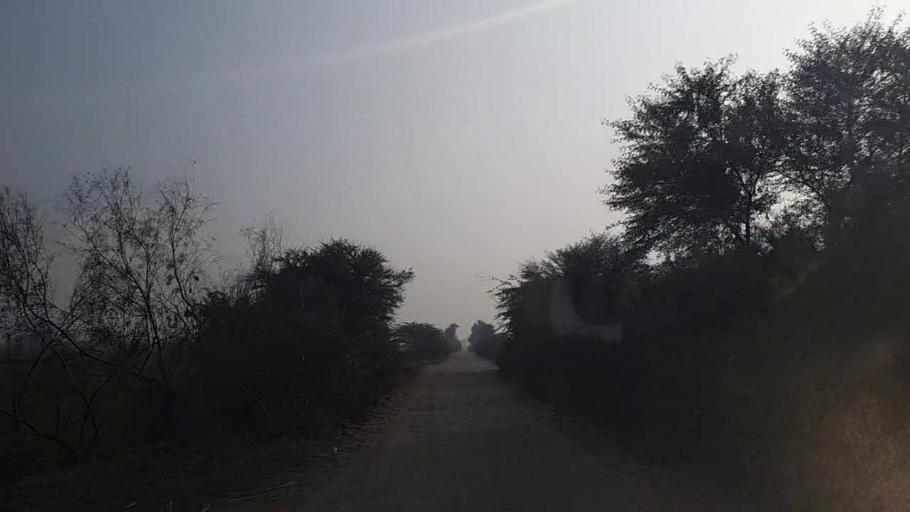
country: PK
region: Sindh
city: Sanghar
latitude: 26.0849
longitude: 68.9203
